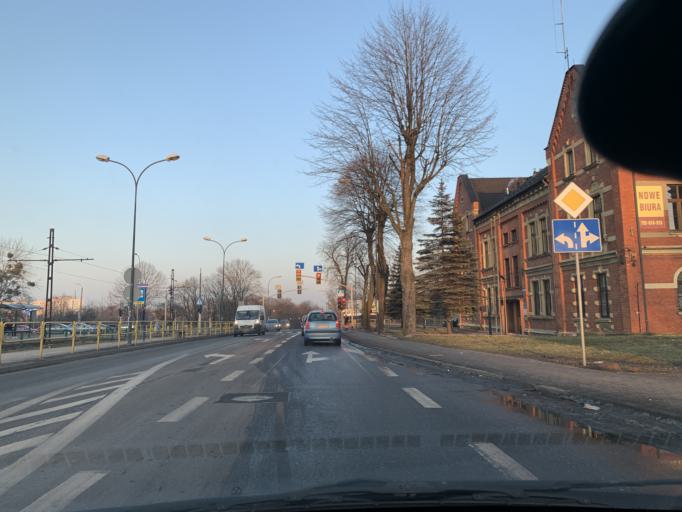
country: PL
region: Silesian Voivodeship
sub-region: Bytom
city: Bytom
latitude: 50.3404
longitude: 18.9079
